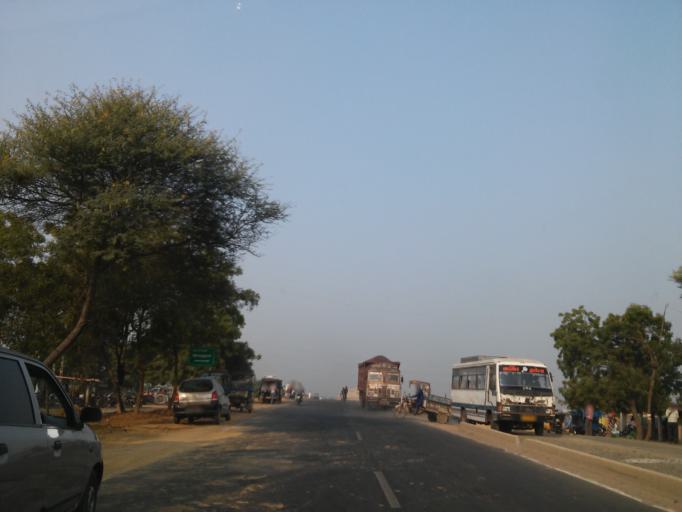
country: IN
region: Gujarat
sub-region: Kachchh
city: Anjar
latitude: 23.2942
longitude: 70.0773
